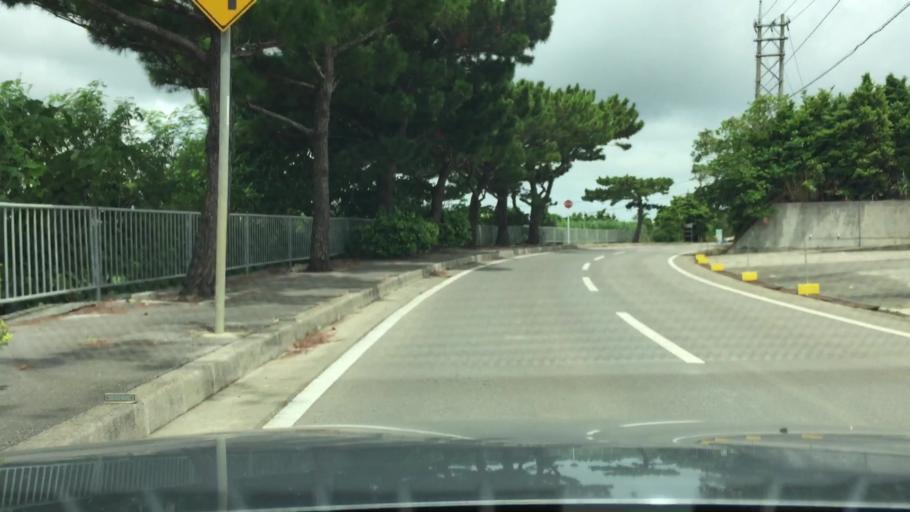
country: JP
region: Okinawa
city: Ishigaki
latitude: 24.3936
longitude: 124.1701
